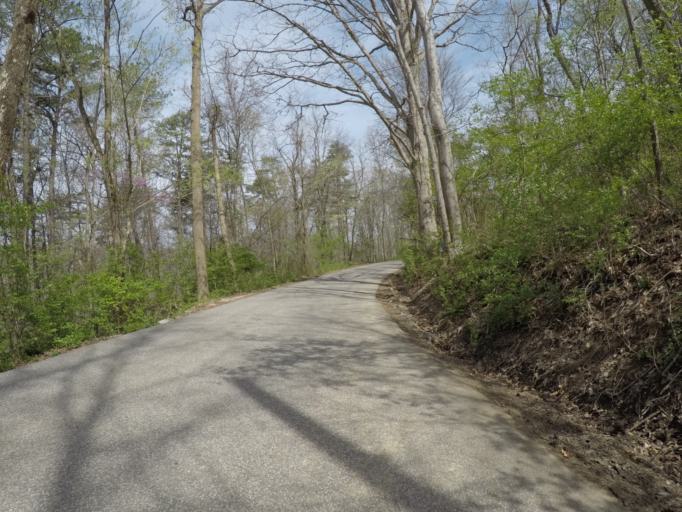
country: US
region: West Virginia
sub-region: Cabell County
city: Pea Ridge
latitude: 38.3421
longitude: -82.3620
